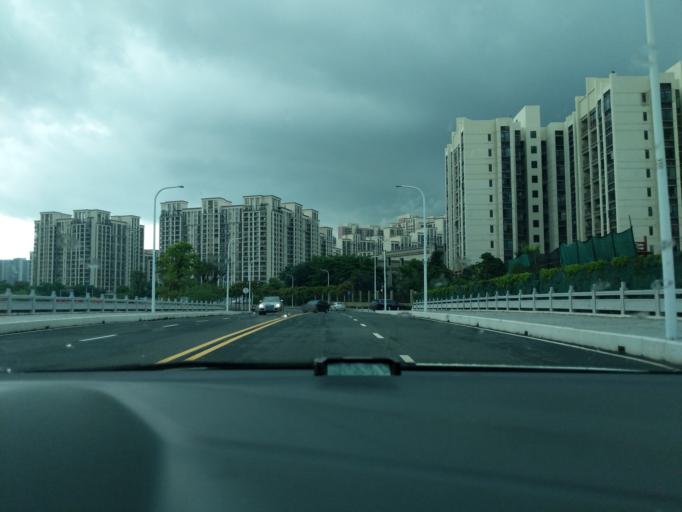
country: CN
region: Guangdong
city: Huangge
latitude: 22.7985
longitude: 113.5169
